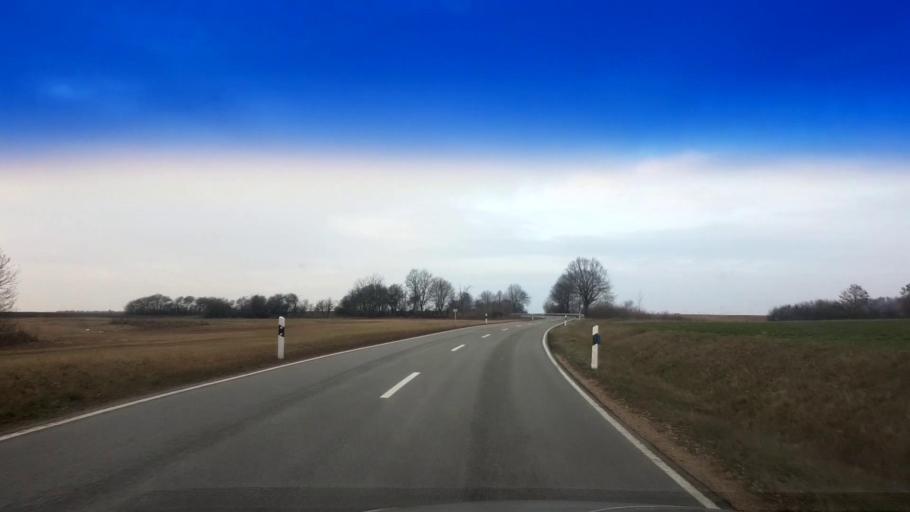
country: DE
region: Bavaria
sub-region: Upper Franconia
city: Hirschaid
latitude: 49.7981
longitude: 10.9881
